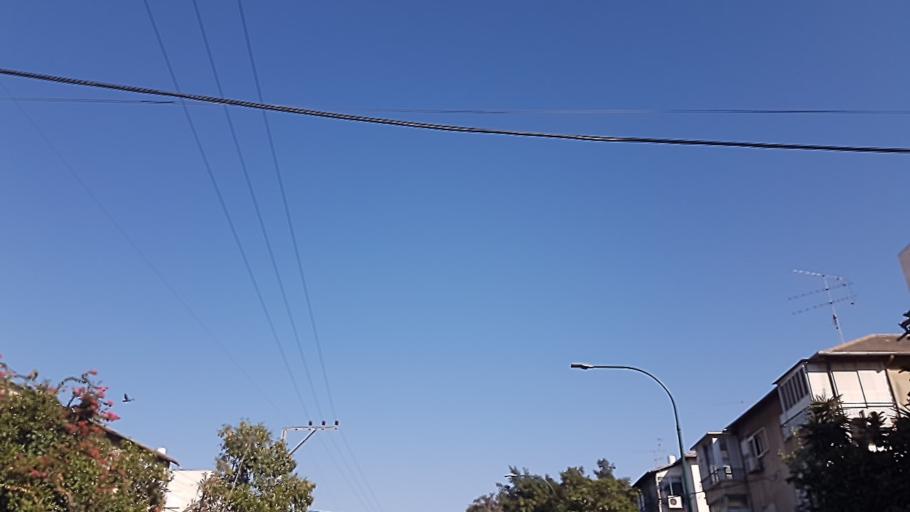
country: IL
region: Tel Aviv
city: Bene Beraq
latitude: 32.0792
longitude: 34.8223
